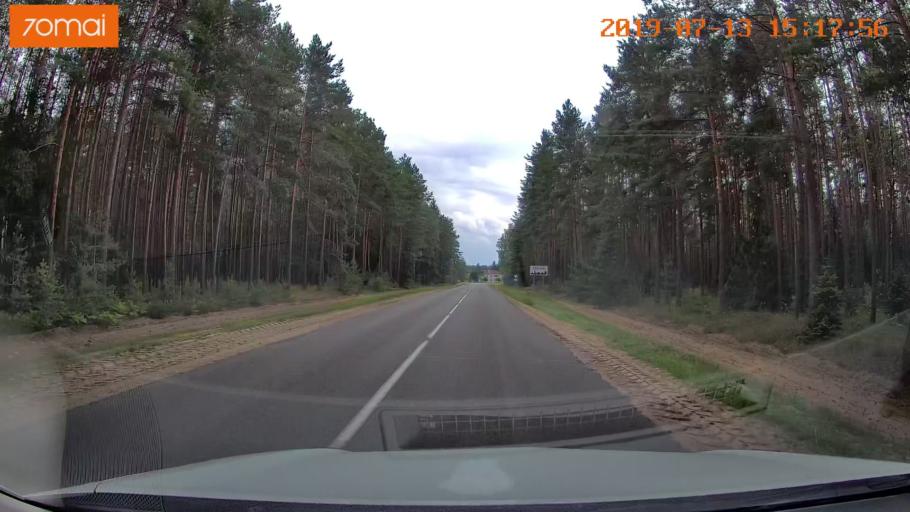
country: BY
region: Mogilev
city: Hlusha
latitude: 53.0896
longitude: 28.8460
